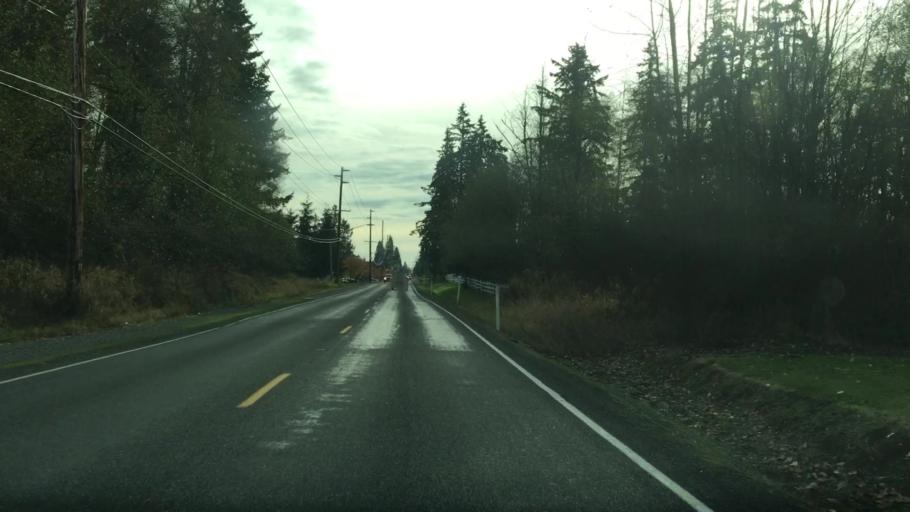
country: US
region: Washington
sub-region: Pierce County
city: South Hill
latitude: 47.1299
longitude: -122.3149
